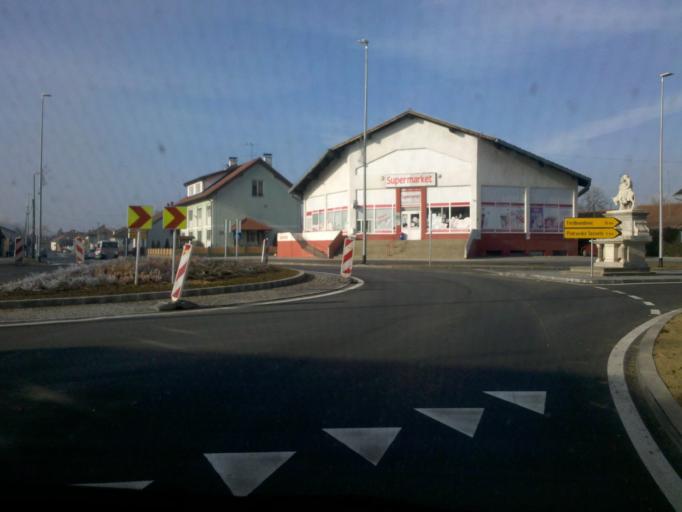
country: HR
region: Koprivnicko-Krizevacka
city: Kalinovac
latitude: 45.9838
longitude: 17.1573
